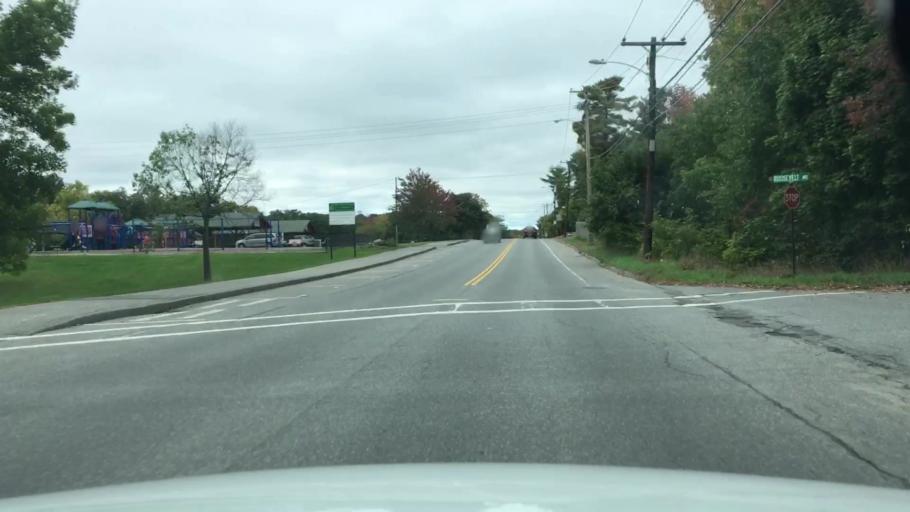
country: US
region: Maine
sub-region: Kennebec County
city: Waterville
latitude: 44.5622
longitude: -69.6447
